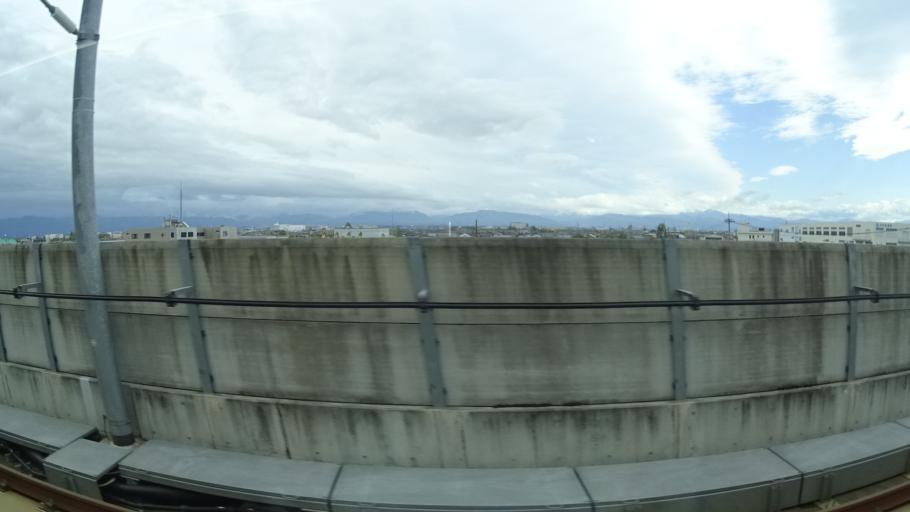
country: JP
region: Toyama
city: Toyama-shi
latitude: 36.7183
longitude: 137.2528
